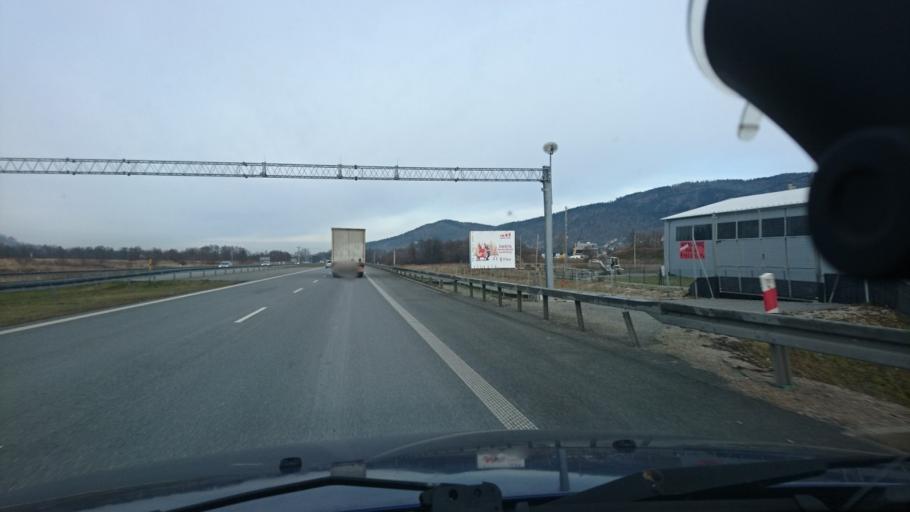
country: PL
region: Silesian Voivodeship
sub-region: Powiat bielski
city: Wilkowice
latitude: 49.7499
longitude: 19.0883
